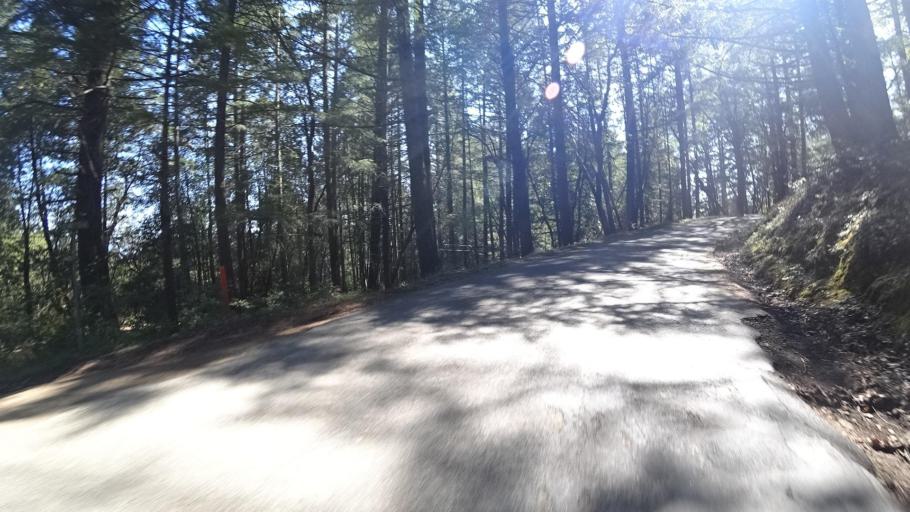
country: US
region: California
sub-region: Humboldt County
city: Redway
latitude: 40.0743
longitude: -123.6514
